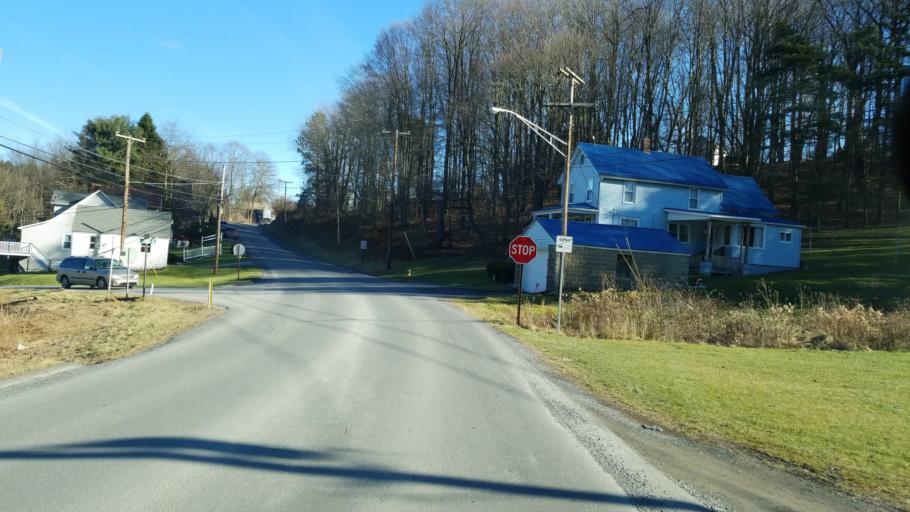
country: US
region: Pennsylvania
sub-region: Clearfield County
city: Sandy
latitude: 41.1242
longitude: -78.7801
